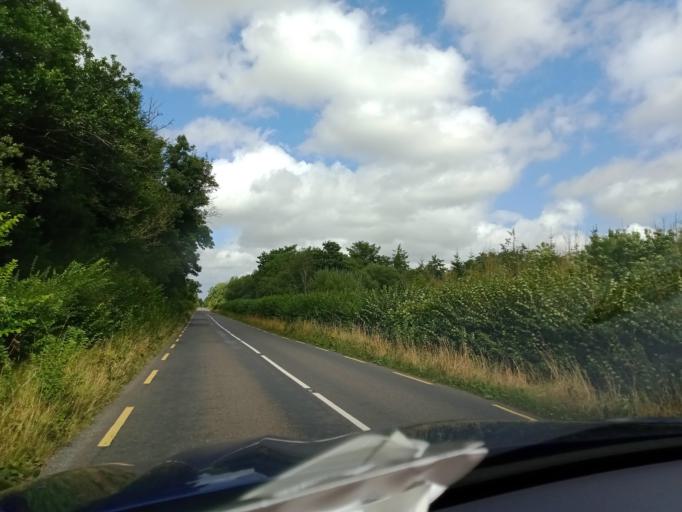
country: IE
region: Leinster
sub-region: Laois
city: Portlaoise
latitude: 52.9823
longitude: -7.2882
